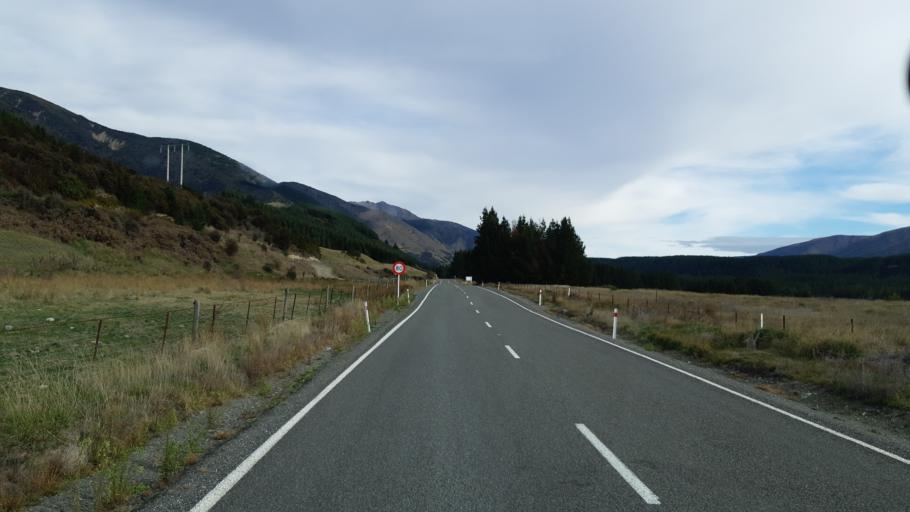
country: NZ
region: Tasman
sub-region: Tasman District
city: Wakefield
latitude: -41.6991
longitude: 173.1315
